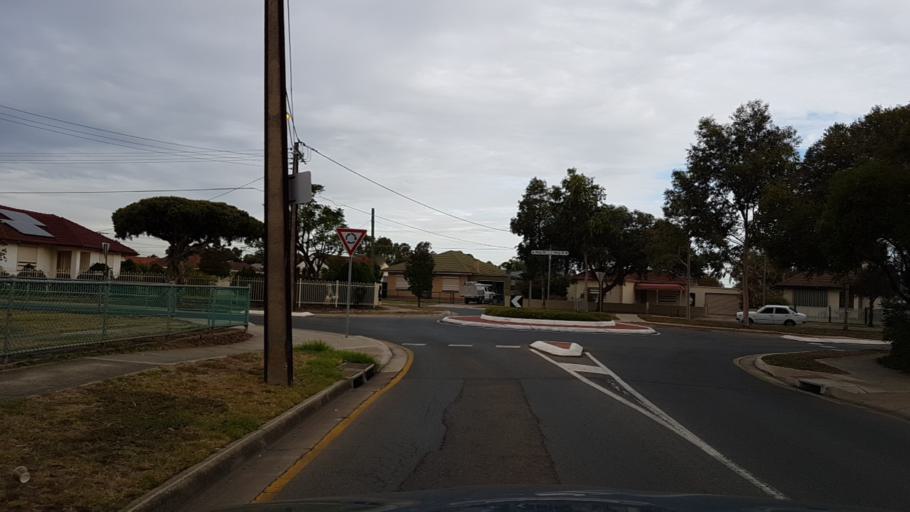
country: AU
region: South Australia
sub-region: Port Adelaide Enfield
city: Alberton
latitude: -34.8588
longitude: 138.5333
